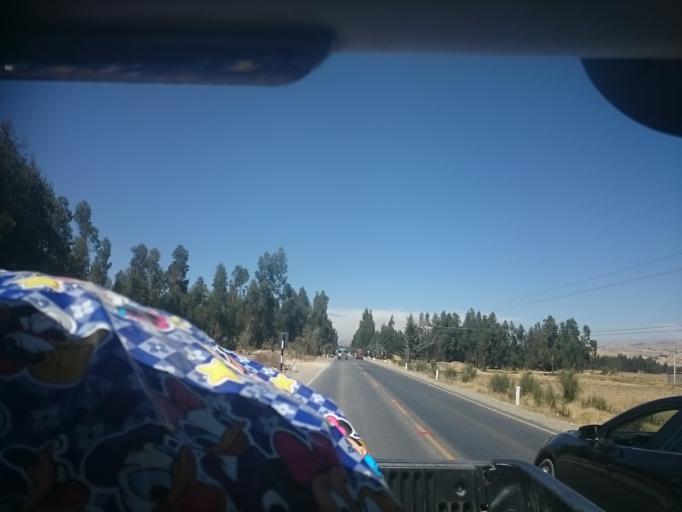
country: PE
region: Junin
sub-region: Provincia de Jauja
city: San Lorenzo
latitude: -11.8601
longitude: -75.3757
